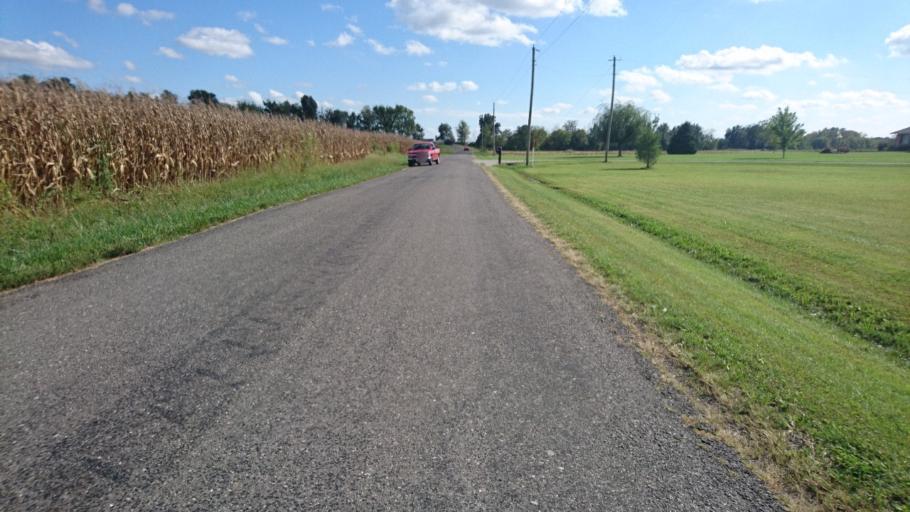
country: US
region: Illinois
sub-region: Macoupin County
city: Staunton
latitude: 38.9924
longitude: -89.7317
